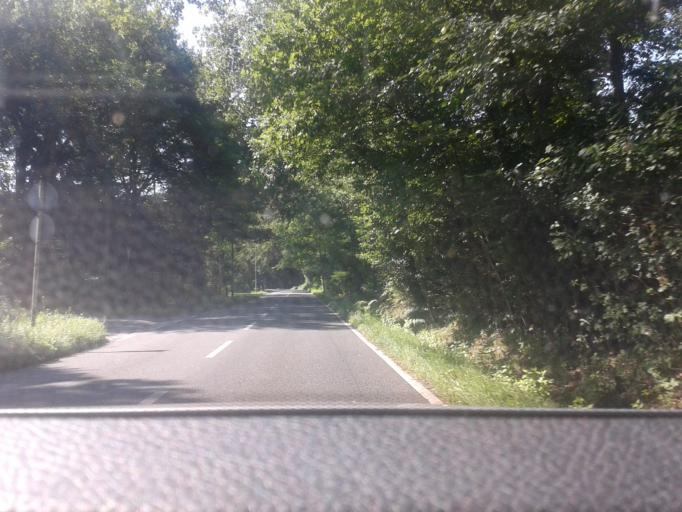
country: DE
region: North Rhine-Westphalia
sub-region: Regierungsbezirk Dusseldorf
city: Muelheim (Ruhr)
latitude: 51.4026
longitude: 6.8445
